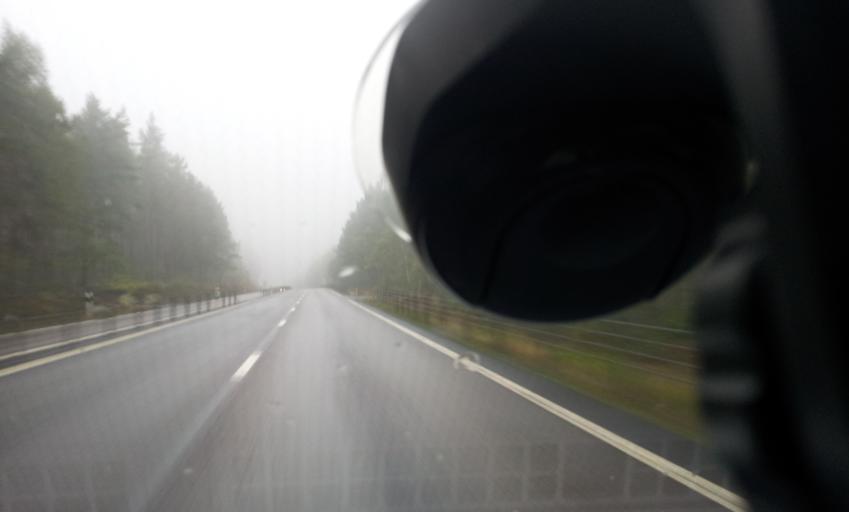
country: SE
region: Kalmar
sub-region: Vasterviks Kommun
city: Gamleby
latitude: 57.8228
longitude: 16.4633
